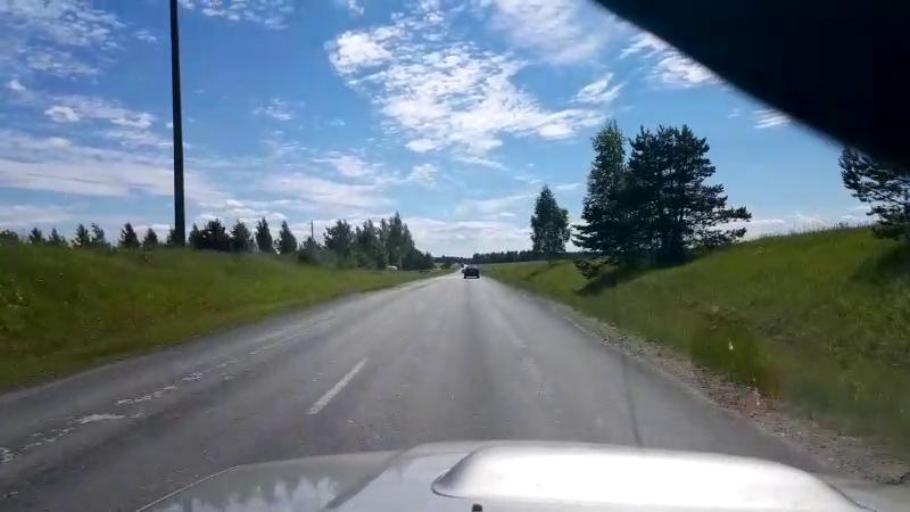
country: EE
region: Jogevamaa
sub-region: Jogeva linn
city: Jogeva
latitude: 58.8383
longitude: 26.2901
